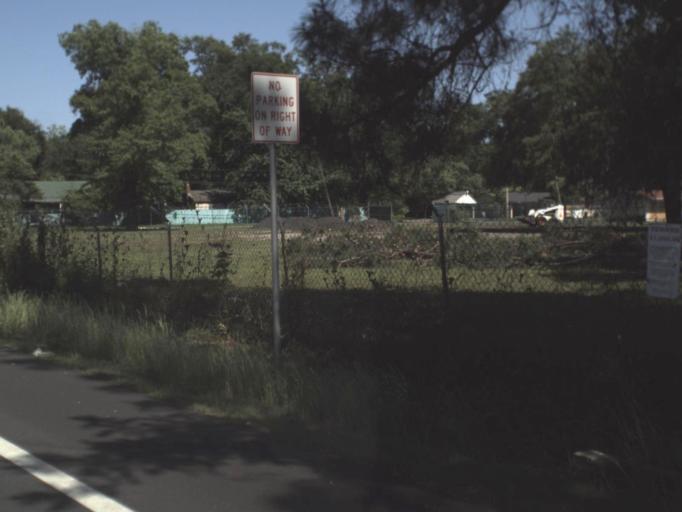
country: US
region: Florida
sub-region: Duval County
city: Jacksonville
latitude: 30.3224
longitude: -81.7868
